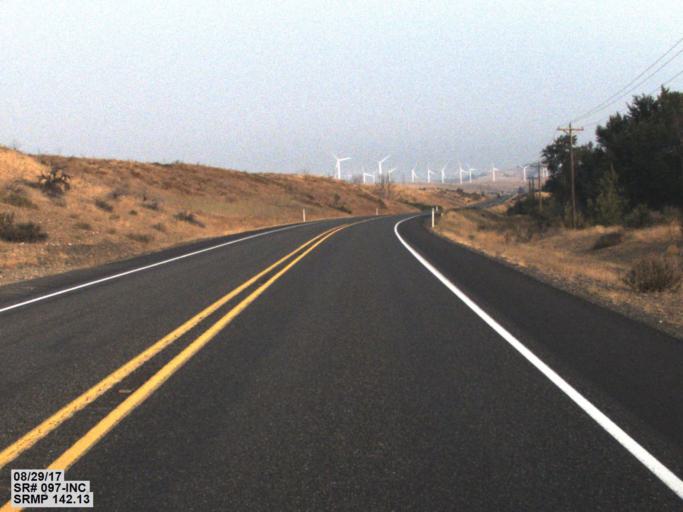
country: US
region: Washington
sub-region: Kittitas County
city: Ellensburg
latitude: 47.1038
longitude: -120.6626
